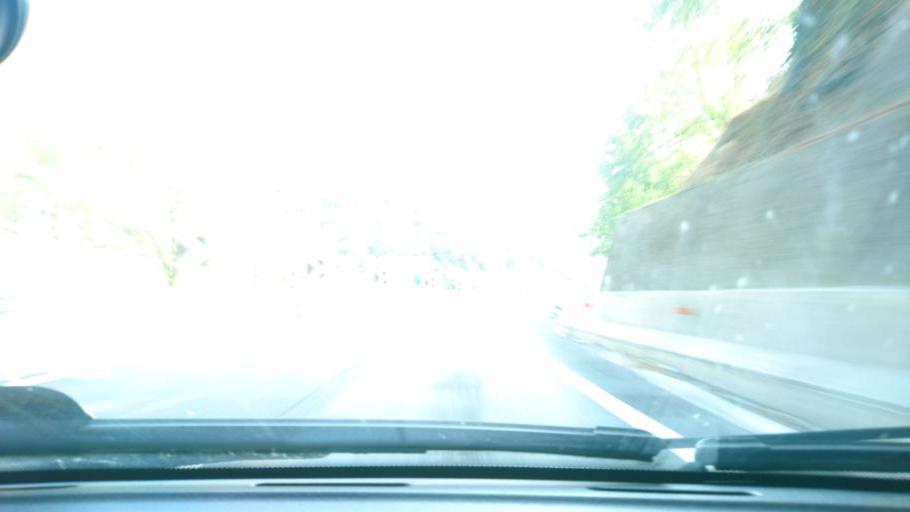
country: IT
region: Liguria
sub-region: Provincia di Savona
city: Quiliano
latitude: 44.3137
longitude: 8.3883
